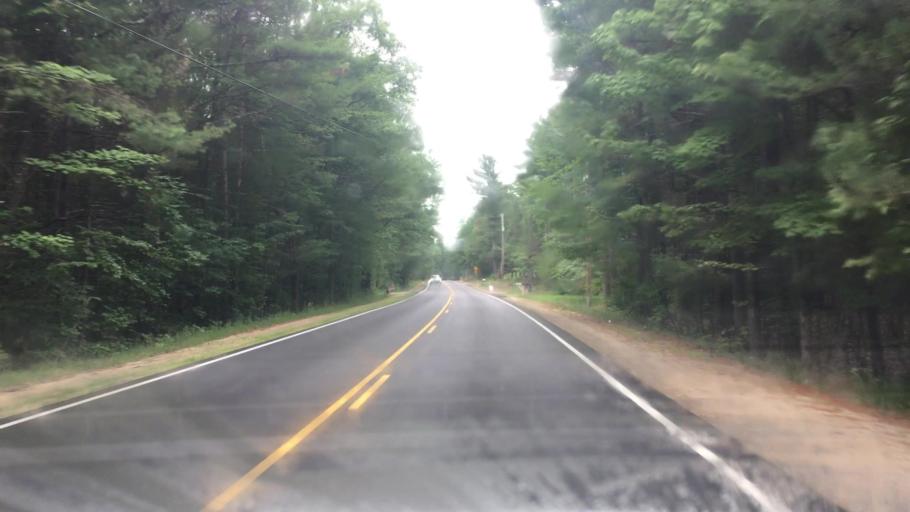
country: US
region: New York
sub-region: Clinton County
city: Morrisonville
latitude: 44.6271
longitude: -73.5873
